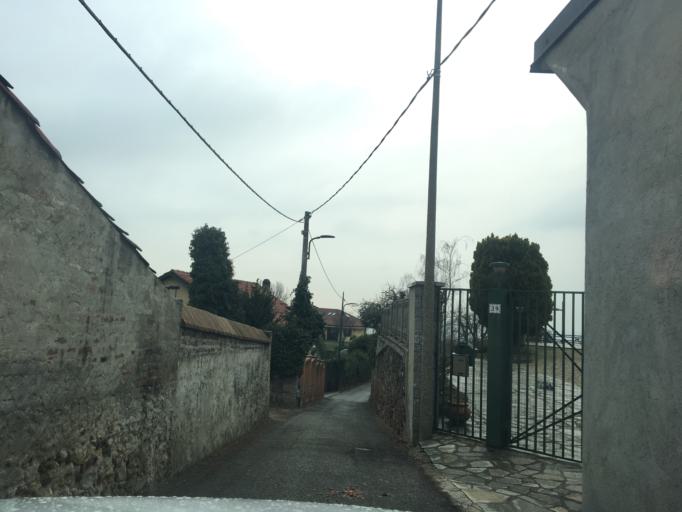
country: IT
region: Piedmont
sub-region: Provincia di Torino
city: Moncalieri
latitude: 45.0265
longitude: 7.6813
